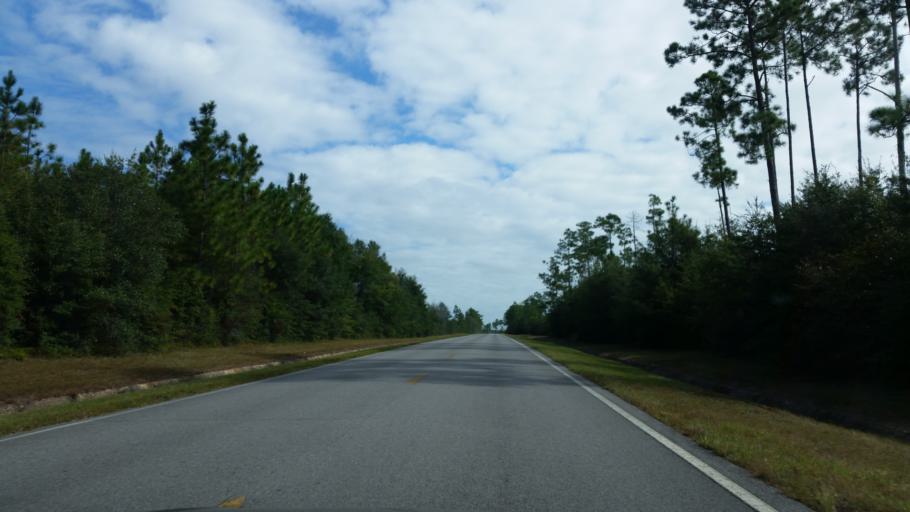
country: US
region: Florida
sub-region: Santa Rosa County
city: Point Baker
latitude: 30.7207
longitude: -86.9601
